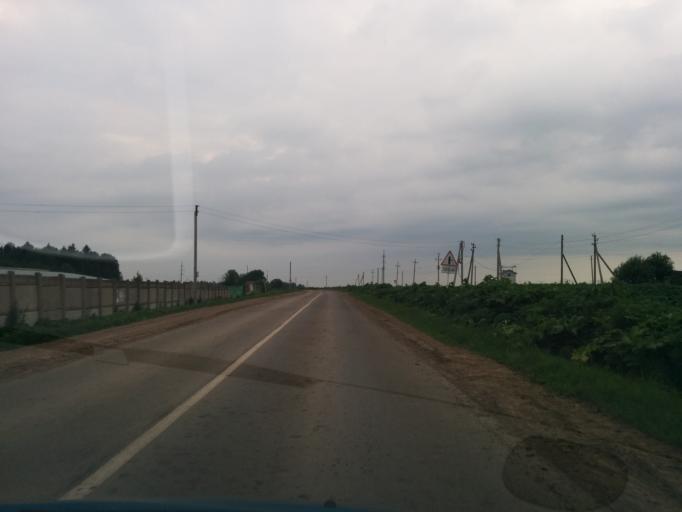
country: RU
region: Perm
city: Polazna
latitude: 58.2196
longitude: 56.2965
